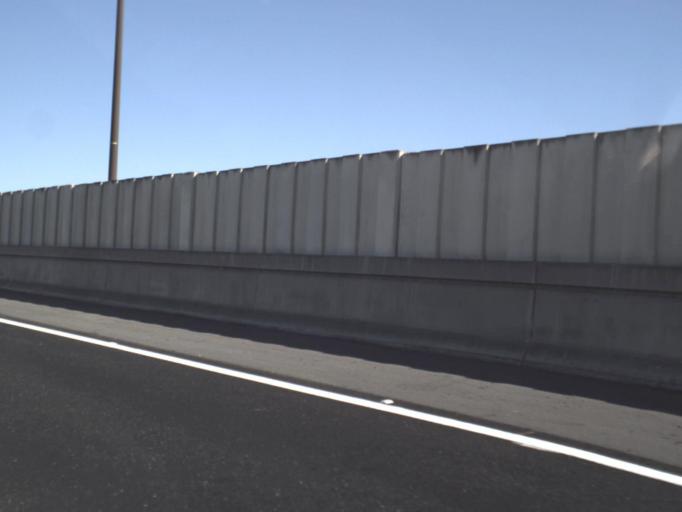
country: US
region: Florida
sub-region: Hillsborough County
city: Cheval
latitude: 28.1550
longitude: -82.5378
